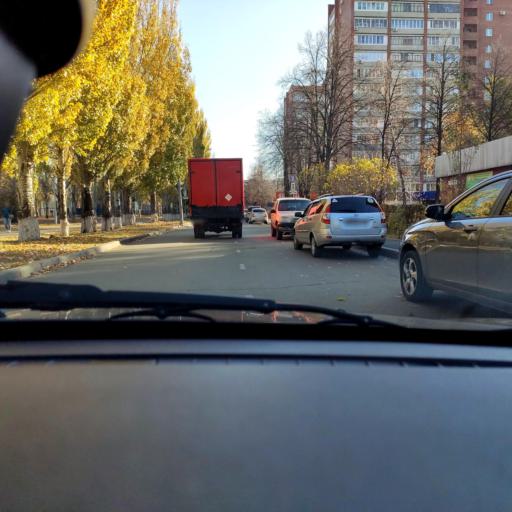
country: RU
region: Samara
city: Tol'yatti
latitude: 53.5236
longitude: 49.2871
